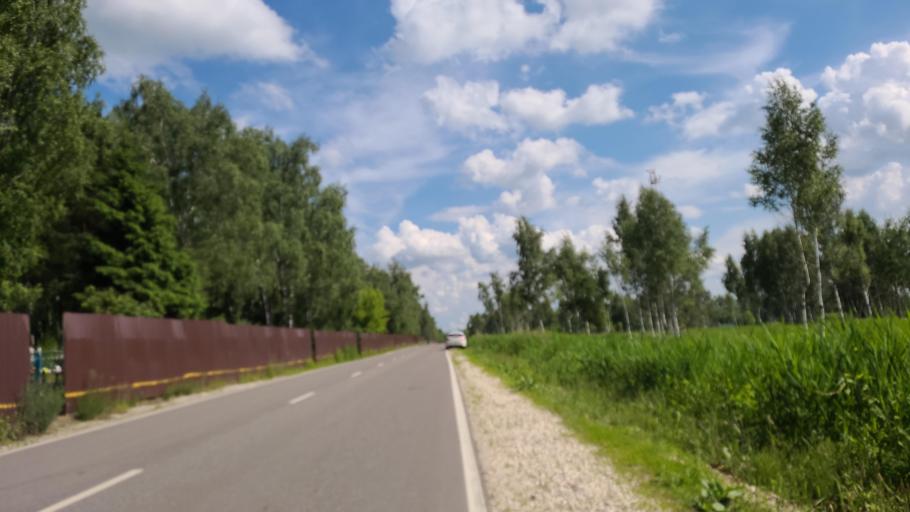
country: RU
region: Moskovskaya
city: Konobeyevo
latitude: 55.4013
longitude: 38.6759
